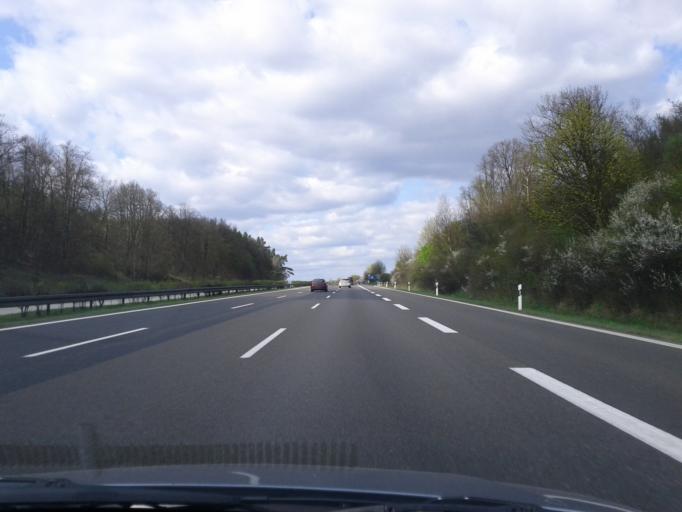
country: DE
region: Brandenburg
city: Grunheide
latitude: 52.4517
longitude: 13.7999
